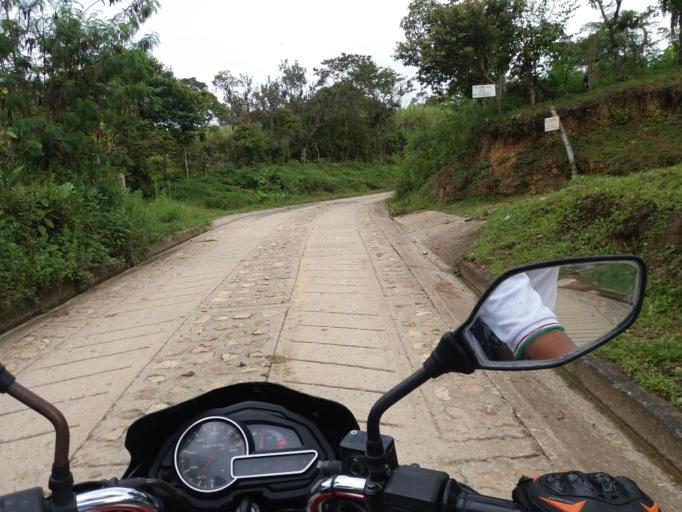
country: CO
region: Santander
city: Guepsa
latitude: 6.0024
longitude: -73.5441
